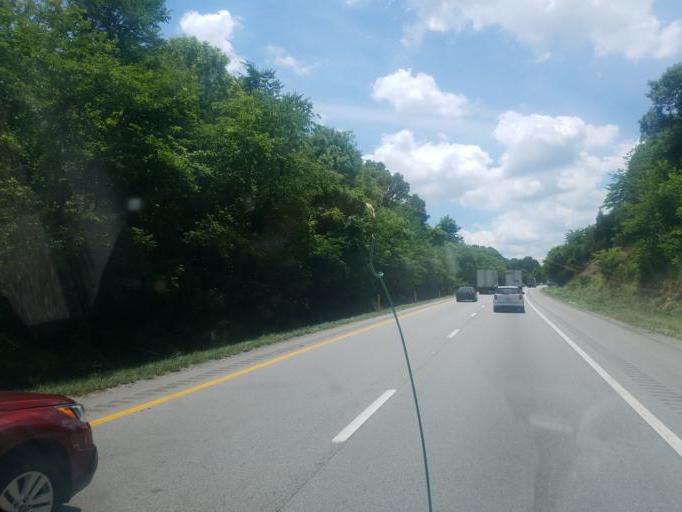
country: US
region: Kentucky
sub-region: Trimble County
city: Providence
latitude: 38.4764
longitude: -85.2733
